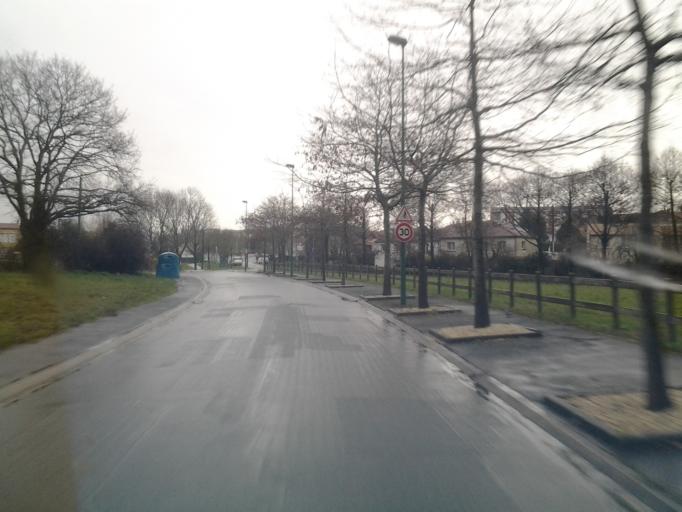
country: FR
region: Pays de la Loire
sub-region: Departement de la Vendee
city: La Roche-sur-Yon
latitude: 46.6768
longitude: -1.4450
